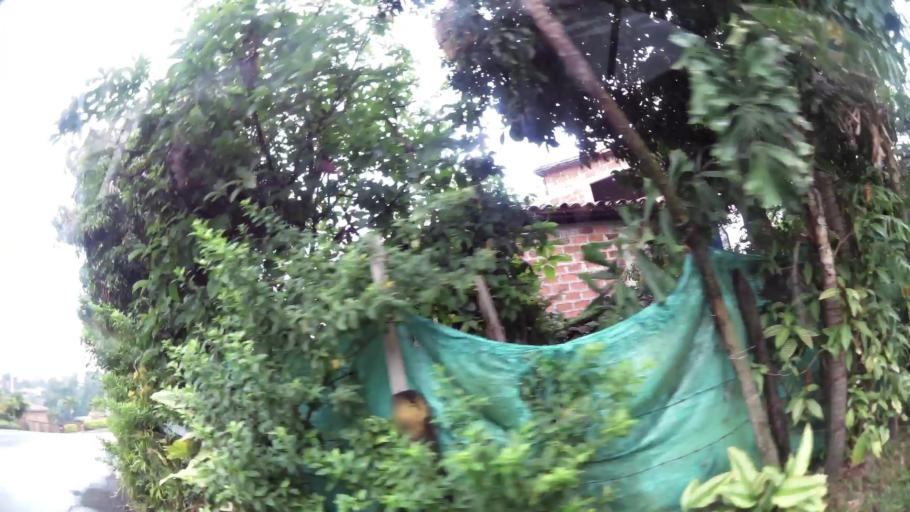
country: CO
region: Antioquia
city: Envigado
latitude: 6.1713
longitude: -75.5650
